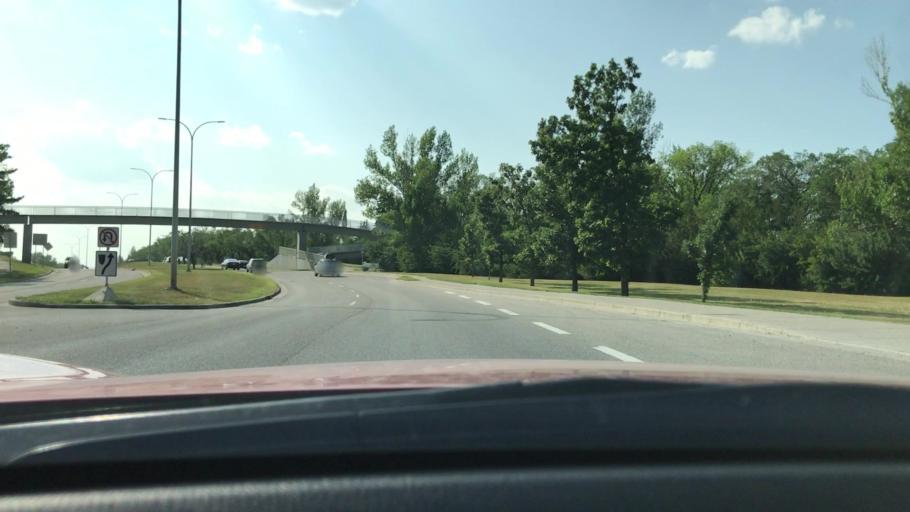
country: CA
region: Alberta
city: Calgary
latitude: 51.0246
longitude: -114.1210
